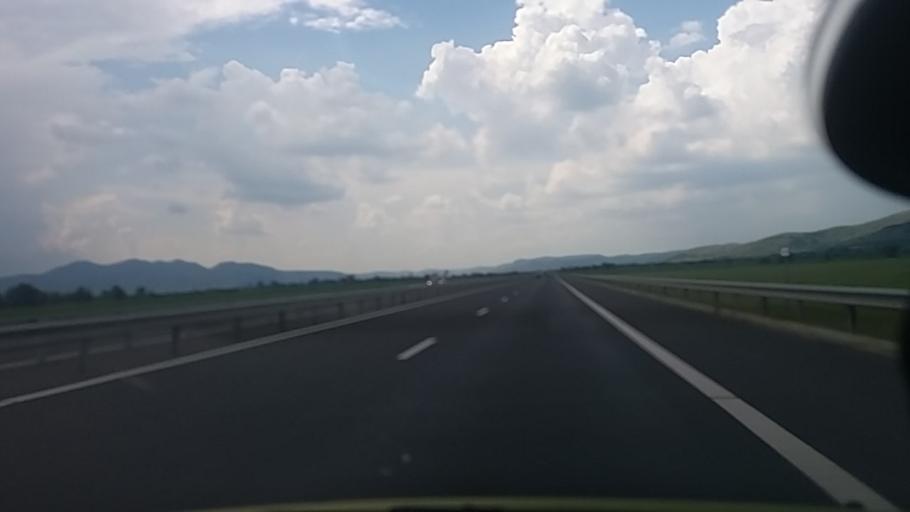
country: RO
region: Hunedoara
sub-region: Oras Simeria
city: Simeria
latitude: 45.8745
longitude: 23.0079
